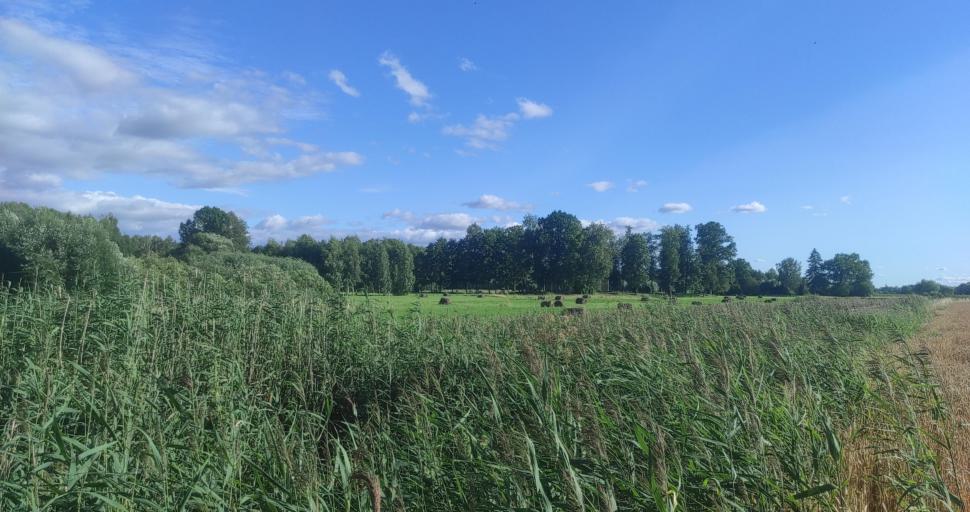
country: LV
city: Tireli
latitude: 56.7061
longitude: 23.4559
